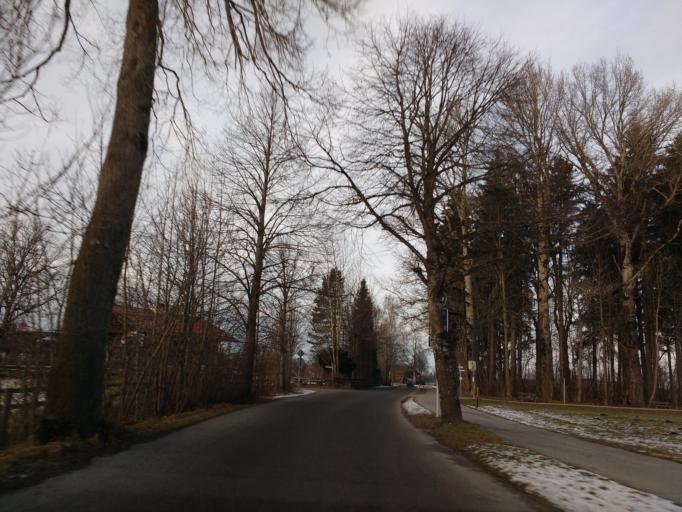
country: DE
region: Bavaria
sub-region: Swabia
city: Schwangau
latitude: 47.5680
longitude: 10.7377
